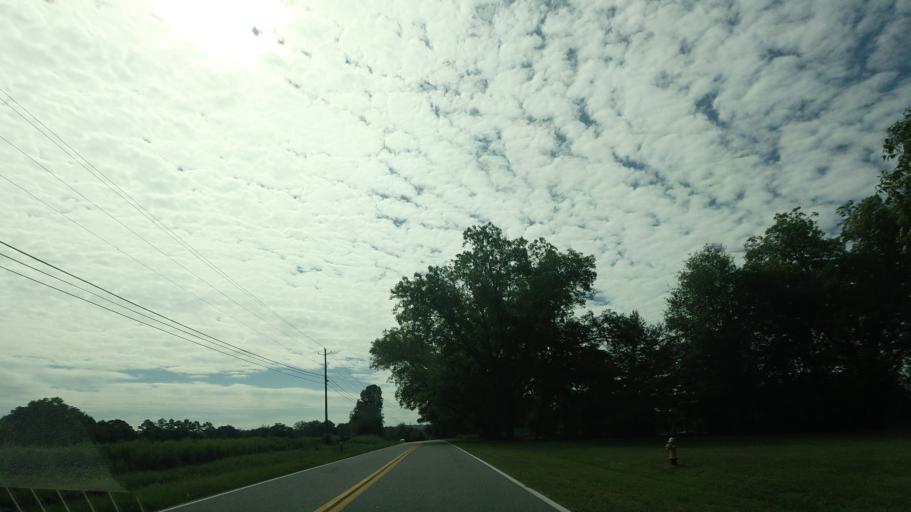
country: US
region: Georgia
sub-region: Peach County
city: Byron
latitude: 32.7026
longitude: -83.7075
